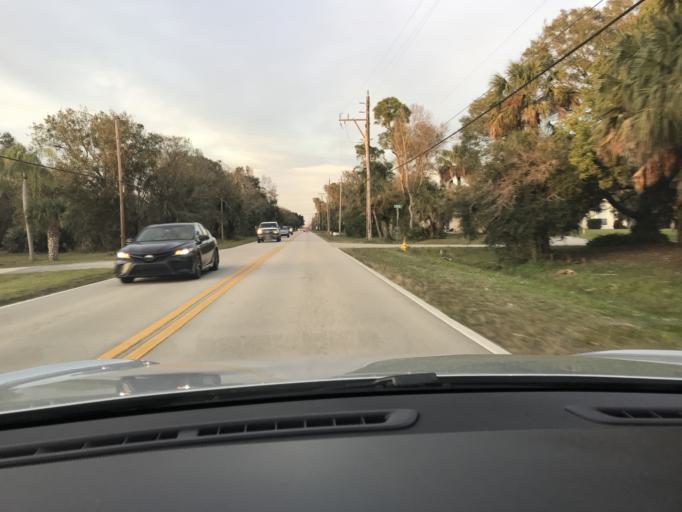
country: US
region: Florida
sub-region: Indian River County
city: Vero Beach South
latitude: 27.6252
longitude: -80.4303
